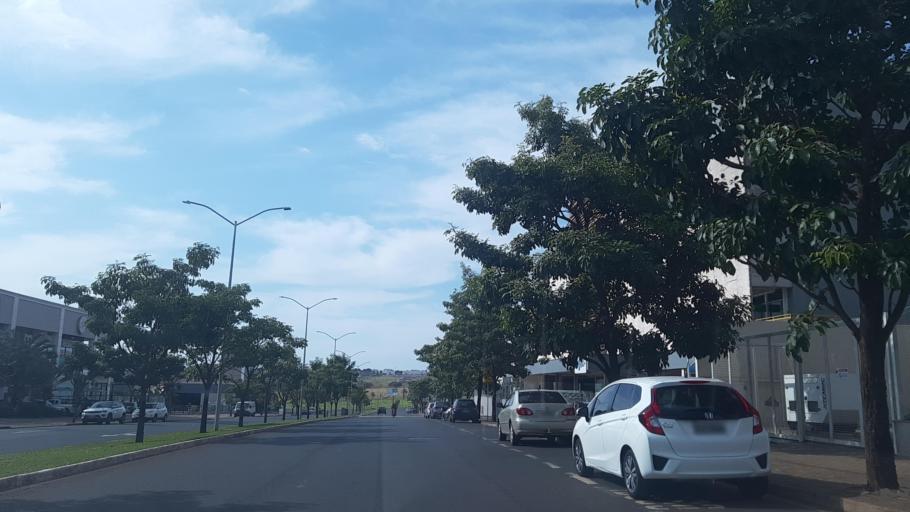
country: BR
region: Minas Gerais
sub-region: Uberlandia
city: Uberlandia
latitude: -18.8794
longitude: -48.2467
